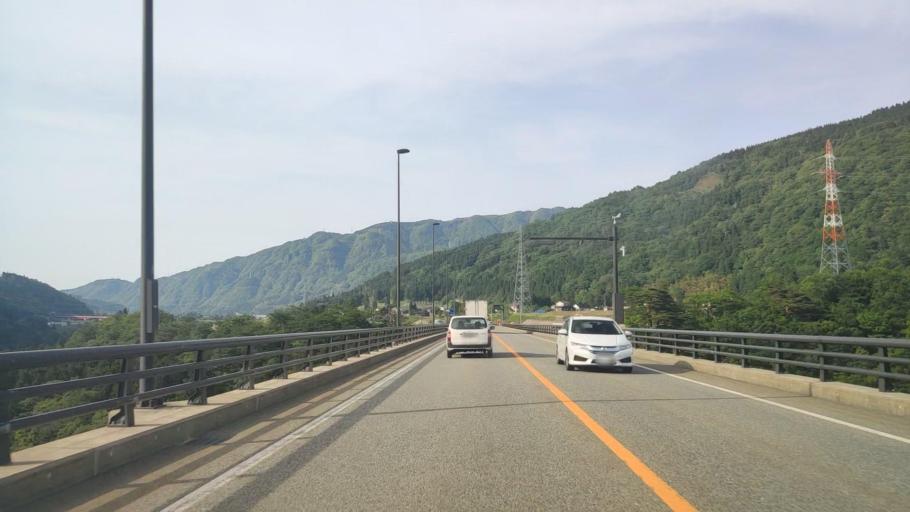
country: JP
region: Toyama
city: Yatsuomachi-higashikumisaka
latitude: 36.5148
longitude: 137.2290
